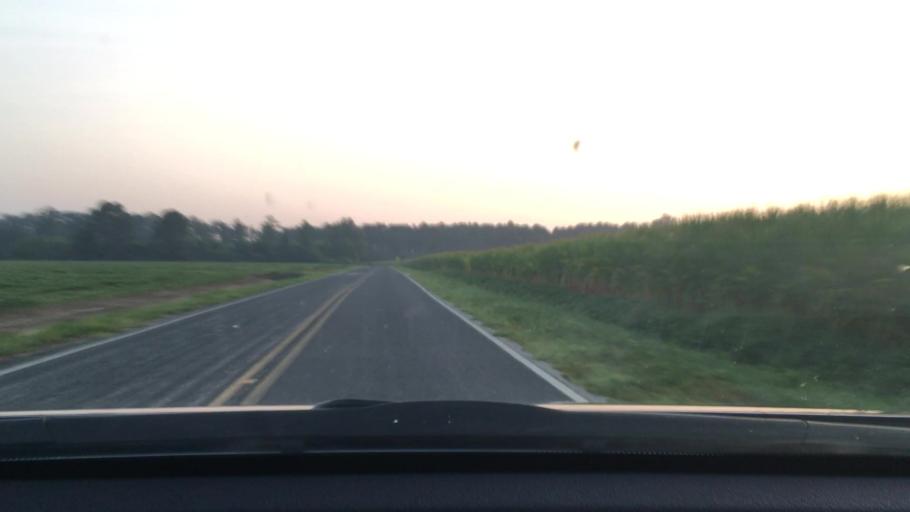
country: US
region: South Carolina
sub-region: Lee County
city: Bishopville
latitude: 34.2252
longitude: -80.1338
